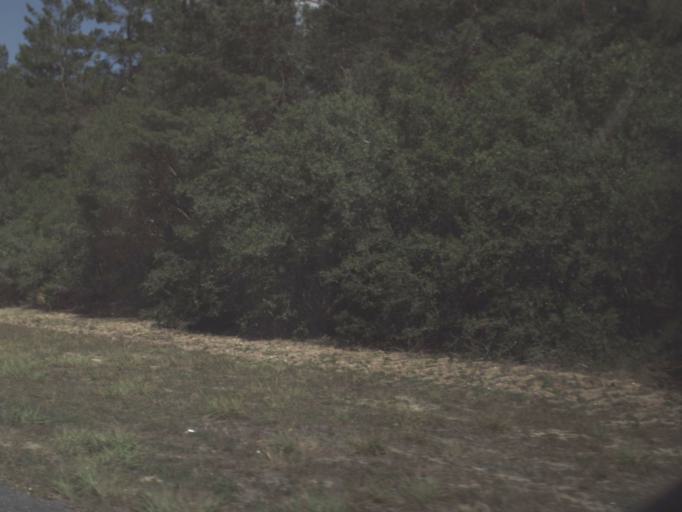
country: US
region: Florida
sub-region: Lake County
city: Astor
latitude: 29.1776
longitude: -81.7538
